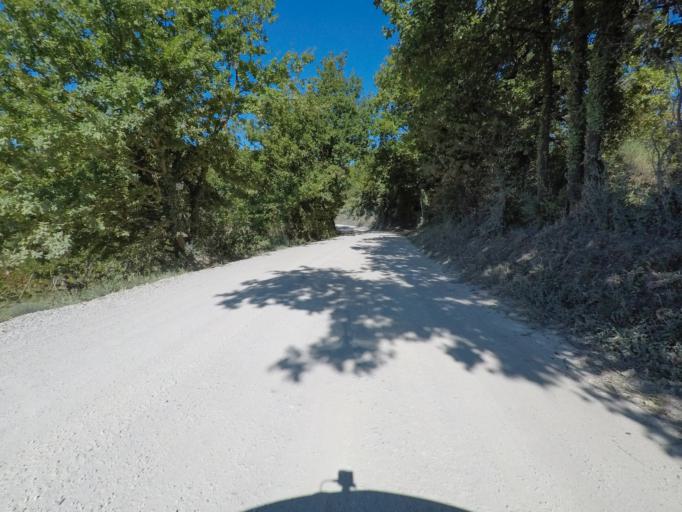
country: IT
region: Tuscany
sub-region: Provincia di Siena
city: Castellina in Chianti
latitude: 43.4395
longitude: 11.3102
